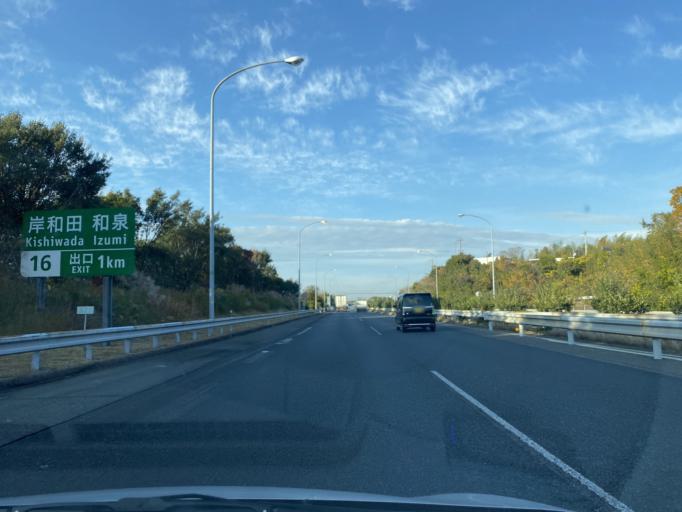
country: JP
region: Osaka
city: Izumi
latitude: 34.4278
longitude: 135.4476
